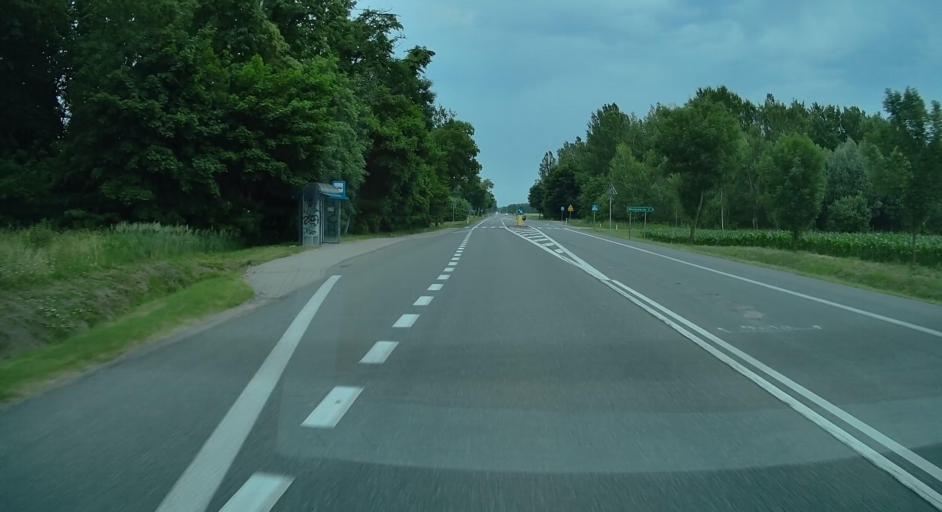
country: PL
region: Lublin Voivodeship
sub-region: Powiat lukowski
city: Trzebieszow
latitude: 52.0571
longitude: 22.5907
